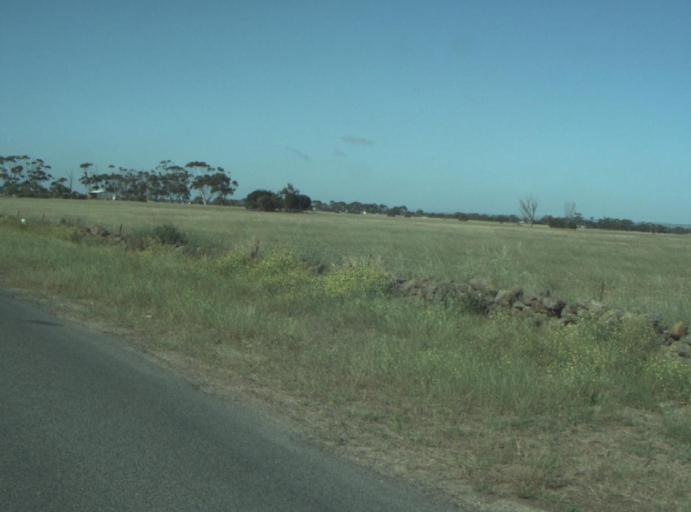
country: AU
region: Victoria
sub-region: Wyndham
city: Little River
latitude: -37.9610
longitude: 144.4634
